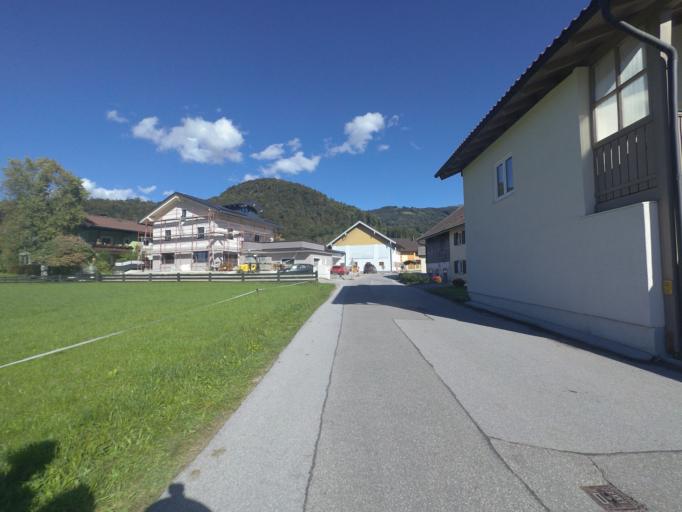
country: AT
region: Salzburg
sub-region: Politischer Bezirk Hallein
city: Adnet
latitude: 47.6888
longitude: 13.1395
